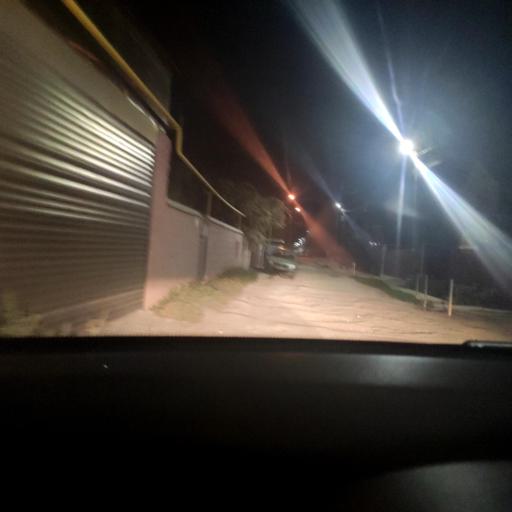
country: RU
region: Samara
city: Samara
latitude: 53.2242
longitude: 50.2188
